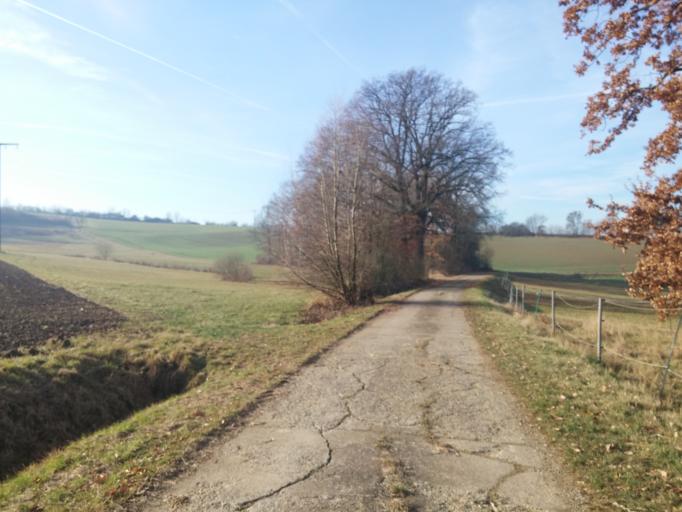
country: DE
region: Bavaria
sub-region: Upper Franconia
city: Grossheirath
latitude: 50.1664
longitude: 10.9620
